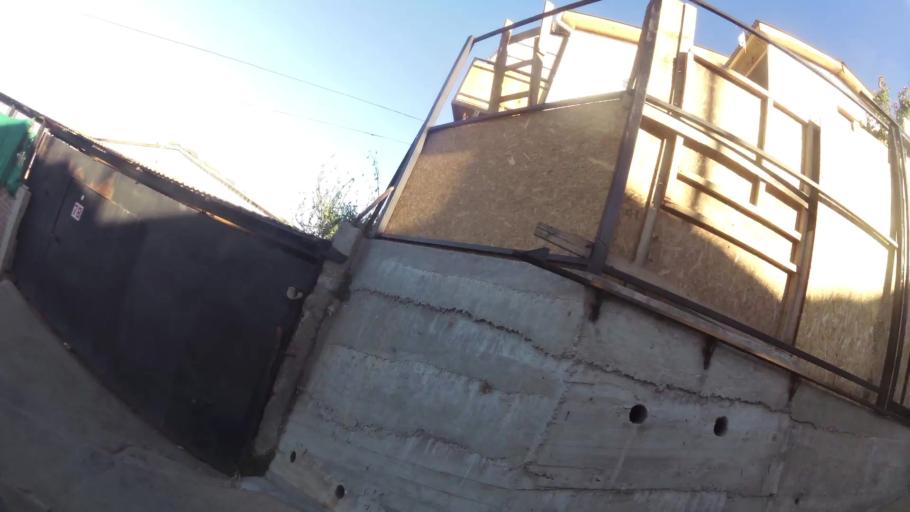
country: CL
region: Valparaiso
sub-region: Provincia de Valparaiso
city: Valparaiso
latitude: -33.0579
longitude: -71.6290
